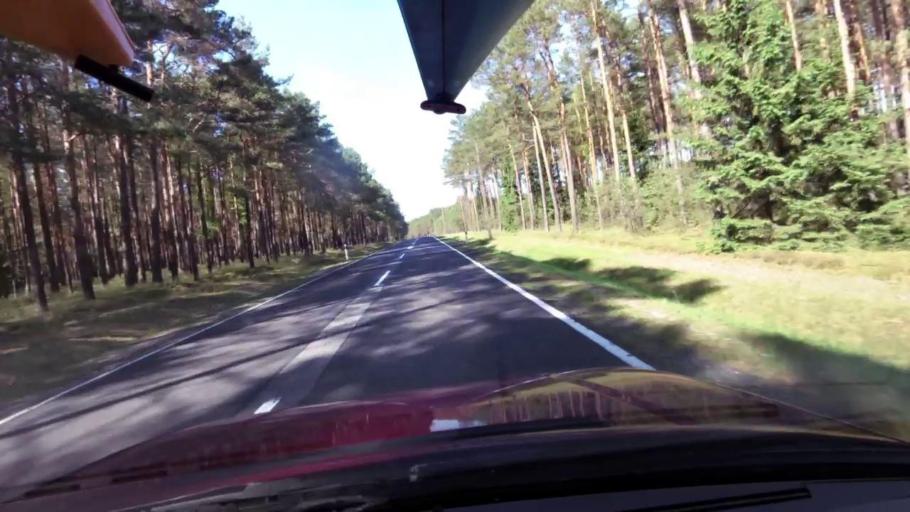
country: PL
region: Pomeranian Voivodeship
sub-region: Powiat bytowski
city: Trzebielino
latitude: 54.1689
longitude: 17.0616
